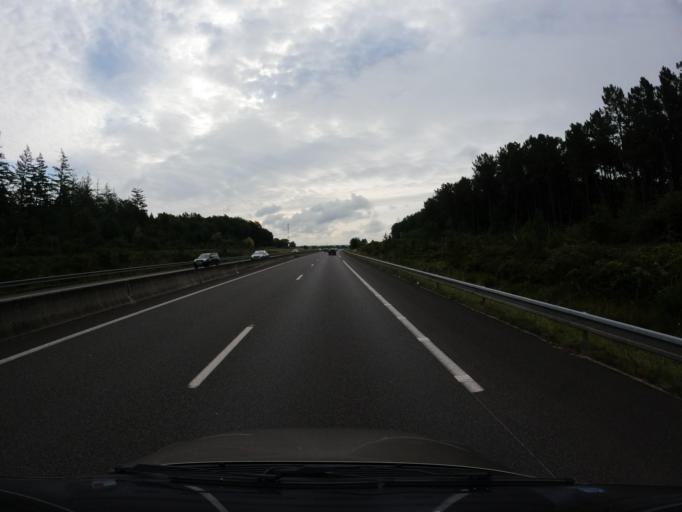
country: FR
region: Centre
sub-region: Departement d'Indre-et-Loire
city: Langeais
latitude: 47.3445
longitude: 0.4121
